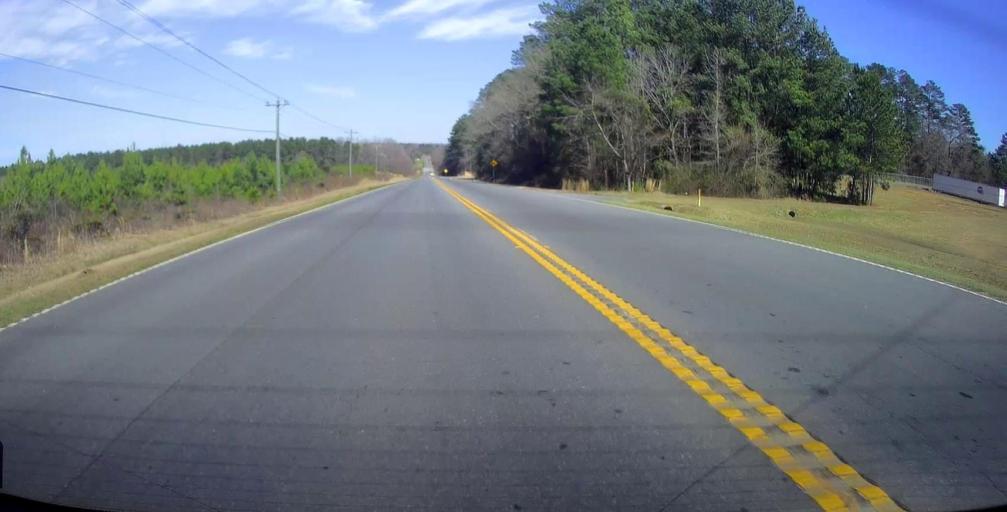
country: US
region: Georgia
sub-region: Houston County
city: Perry
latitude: 32.4467
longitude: -83.6289
